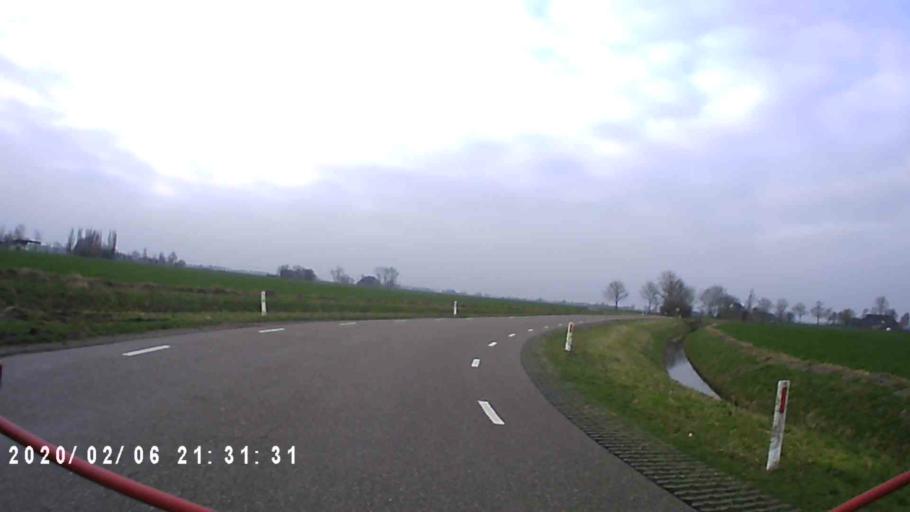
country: NL
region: Groningen
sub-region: Gemeente Zuidhorn
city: Oldehove
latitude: 53.2825
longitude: 6.3888
